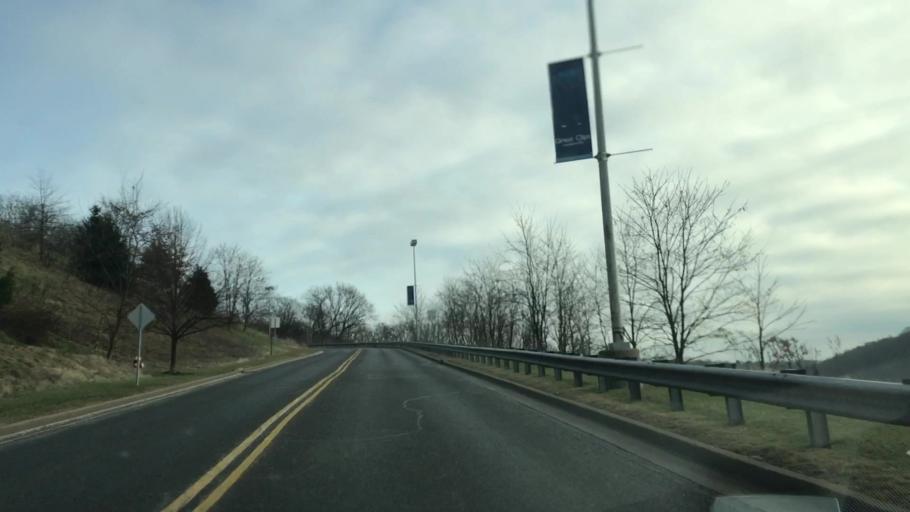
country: US
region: Pennsylvania
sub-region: Allegheny County
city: Ben Avon
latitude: 40.5332
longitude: -80.0661
